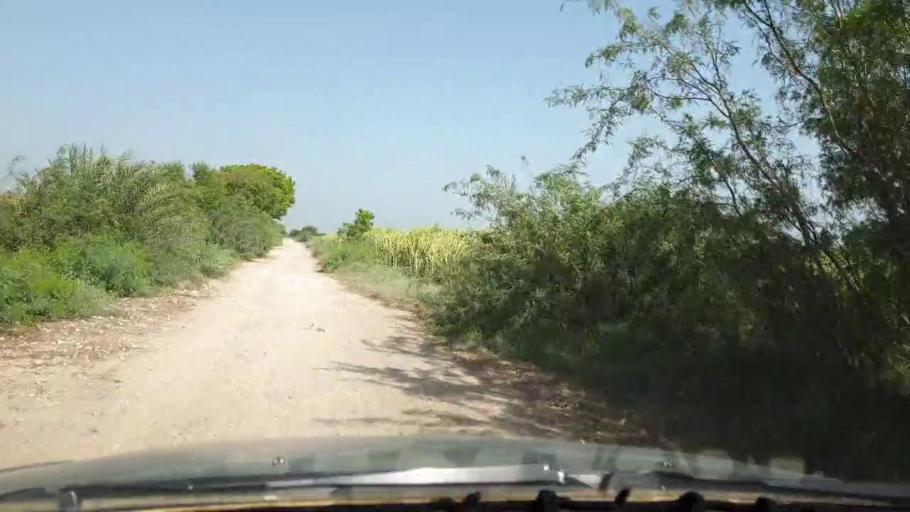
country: PK
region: Sindh
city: Matli
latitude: 25.0865
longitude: 68.6126
